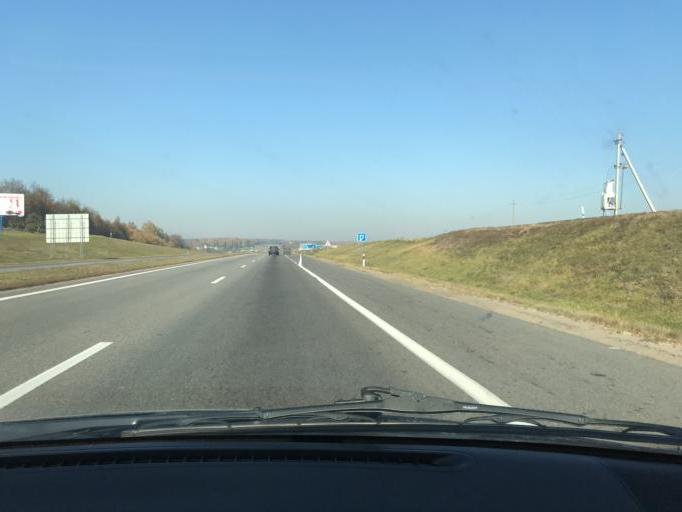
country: BY
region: Minsk
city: Samakhvalavichy
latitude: 53.7338
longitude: 27.5170
